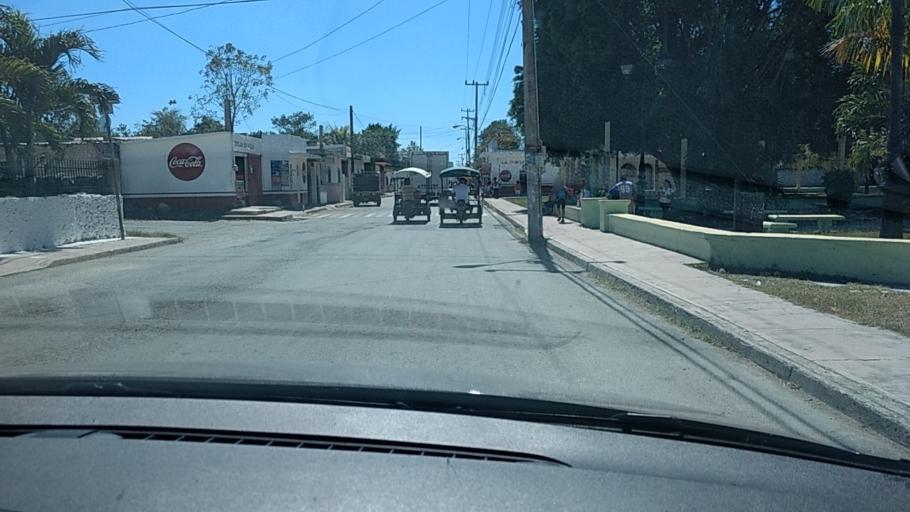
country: MX
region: Yucatan
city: Espita
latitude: 21.0192
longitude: -88.3053
